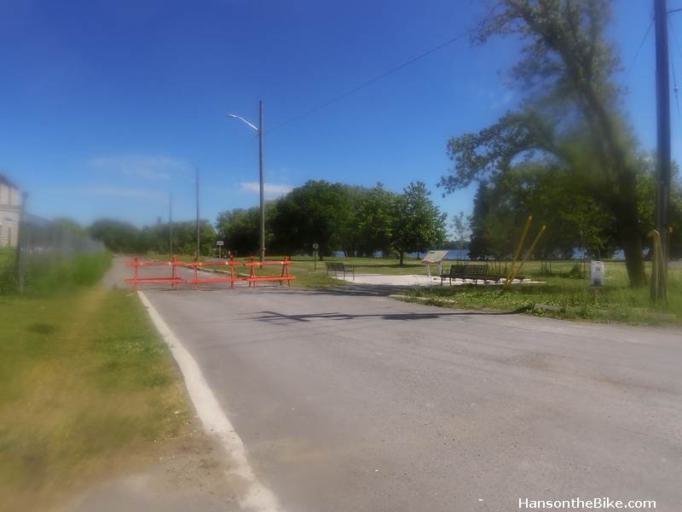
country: CA
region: Ontario
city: Kingston
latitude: 44.2375
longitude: -76.4813
